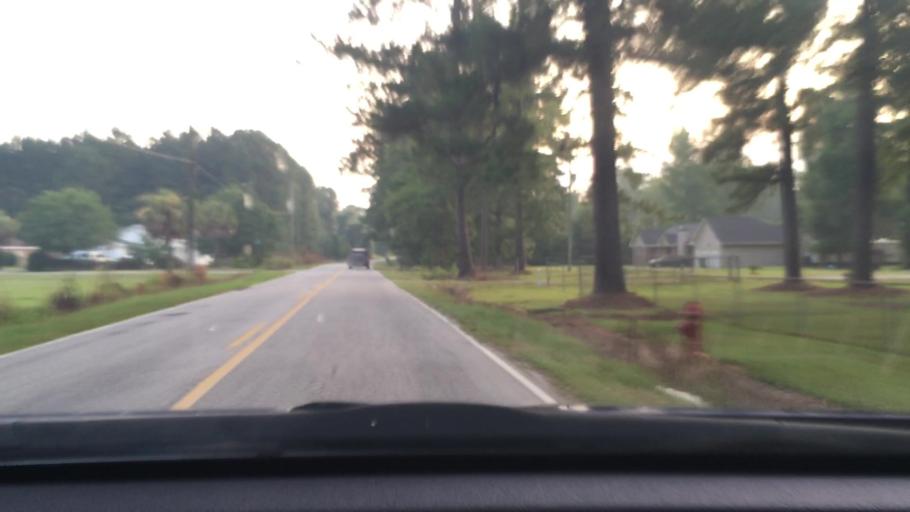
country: US
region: South Carolina
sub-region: Darlington County
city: Hartsville
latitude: 34.3343
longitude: -80.1023
